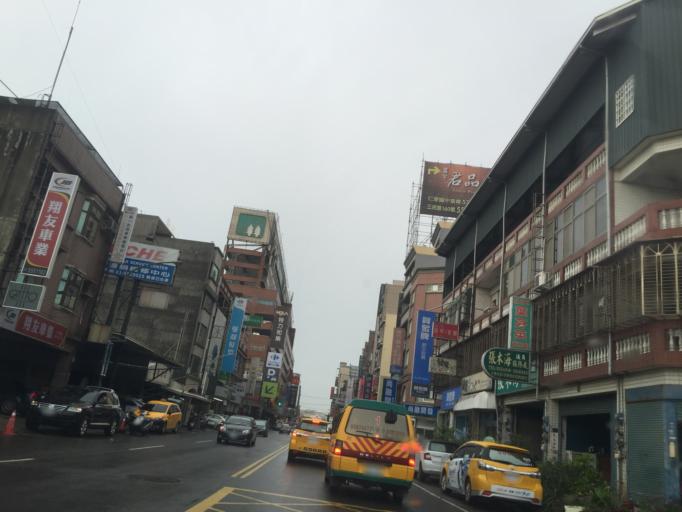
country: TW
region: Taiwan
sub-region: Hsinchu
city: Zhubei
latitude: 24.8247
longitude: 121.0084
